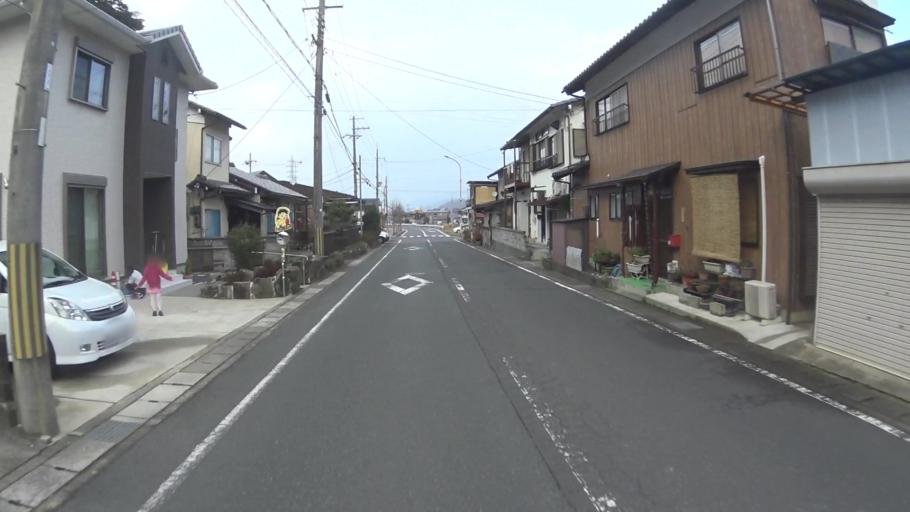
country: JP
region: Kyoto
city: Maizuru
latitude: 35.4488
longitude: 135.3975
